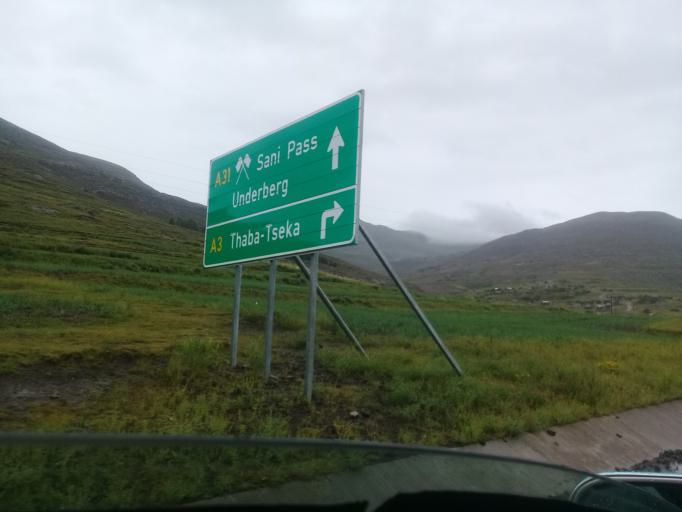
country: LS
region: Mokhotlong
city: Mokhotlong
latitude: -29.3336
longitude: 29.0320
